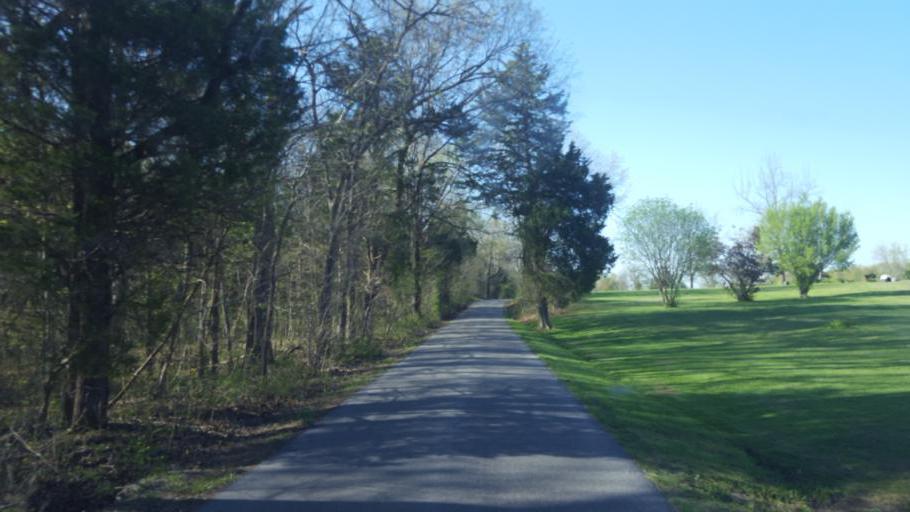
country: US
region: Kentucky
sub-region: Barren County
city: Cave City
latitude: 37.1700
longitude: -86.0426
